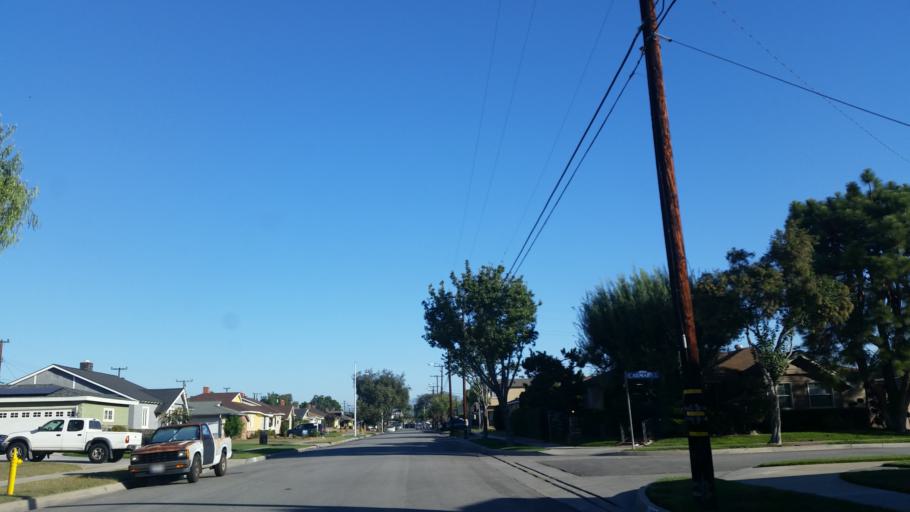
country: US
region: California
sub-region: Los Angeles County
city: Bellflower
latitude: 33.8665
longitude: -118.1114
